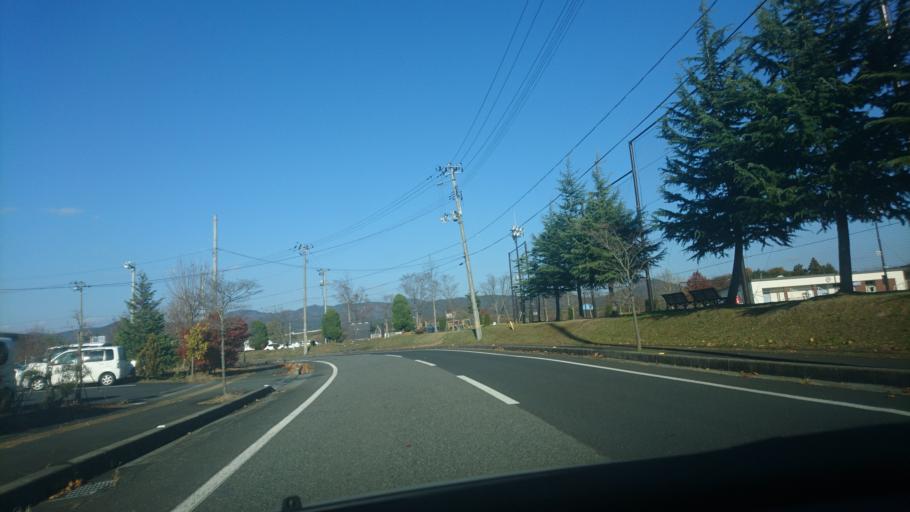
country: JP
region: Iwate
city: Ichinoseki
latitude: 38.9383
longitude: 141.1560
